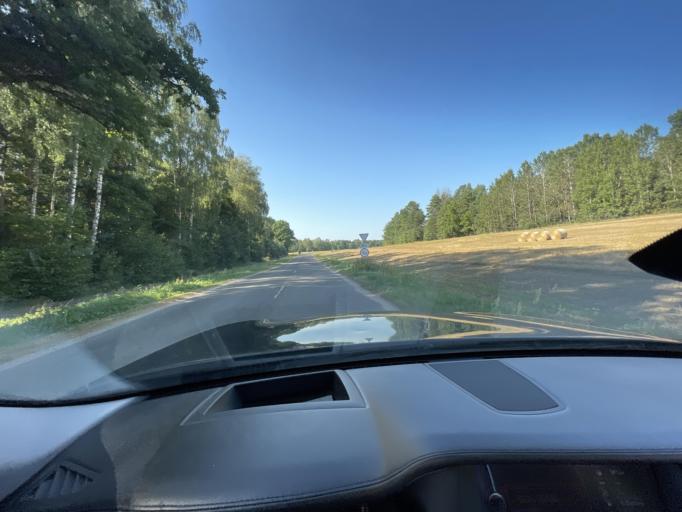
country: BY
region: Grodnenskaya
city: Hrodna
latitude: 53.7581
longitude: 23.9675
